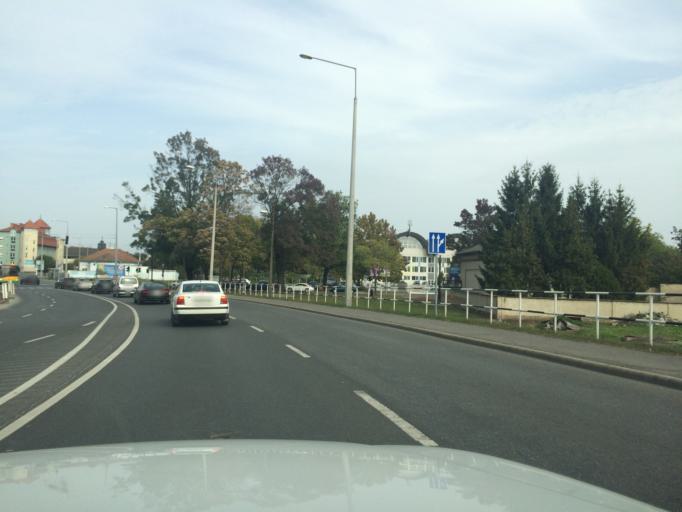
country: HU
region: Szabolcs-Szatmar-Bereg
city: Nyiregyhaza
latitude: 47.9549
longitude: 21.7210
